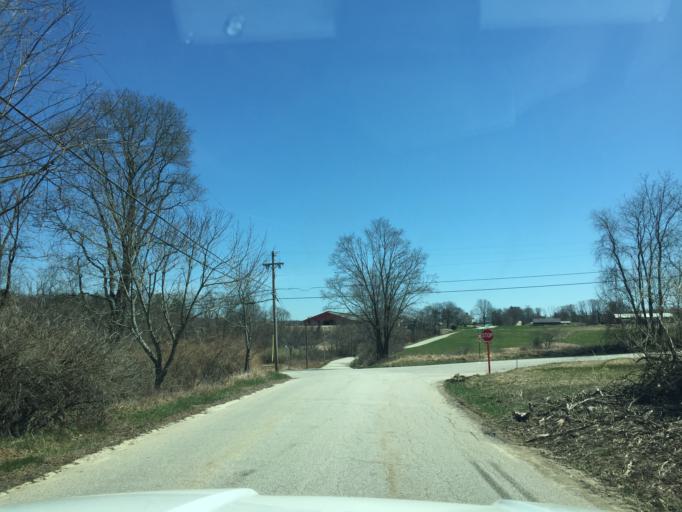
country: US
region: Connecticut
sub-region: Windham County
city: Quinebaug
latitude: 42.0081
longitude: -71.9678
